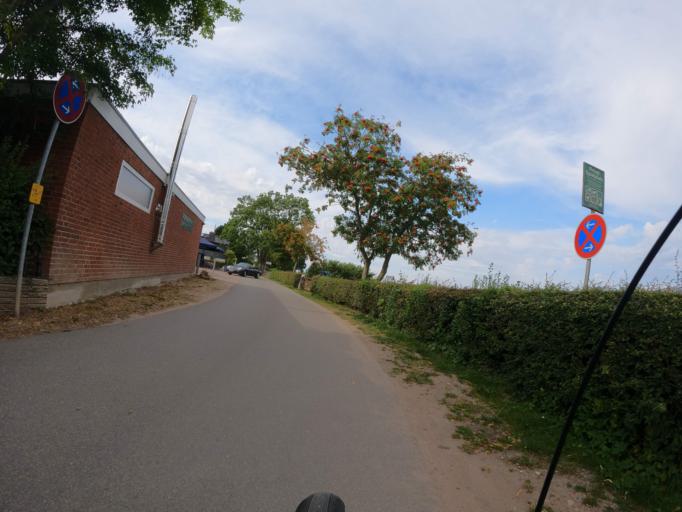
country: DE
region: Schleswig-Holstein
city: Steinberg
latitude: 54.7862
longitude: 9.7989
